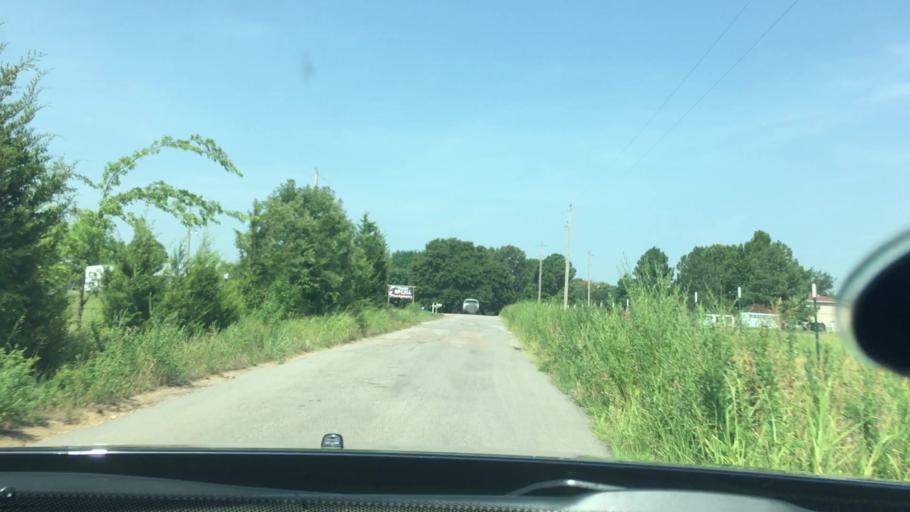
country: US
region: Oklahoma
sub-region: Atoka County
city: Atoka
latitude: 34.3603
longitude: -96.1688
